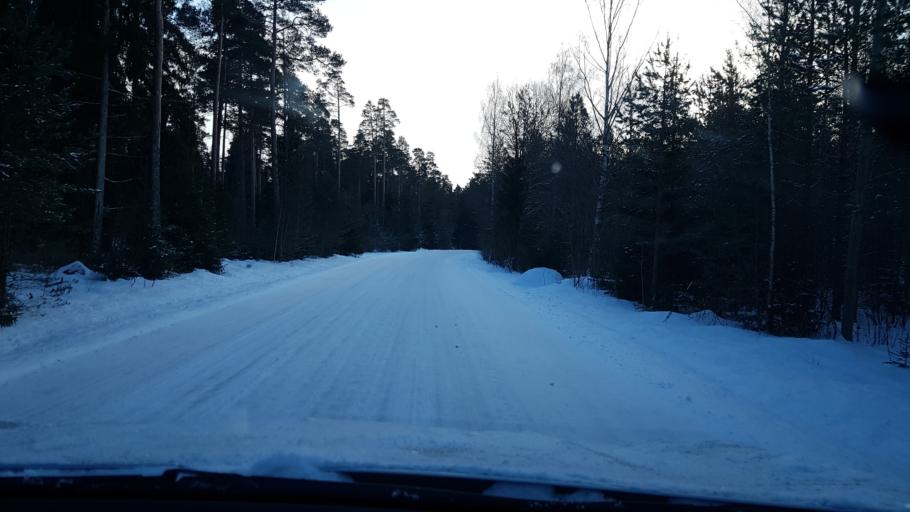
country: EE
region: Harju
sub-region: Nissi vald
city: Turba
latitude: 59.2122
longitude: 24.1413
